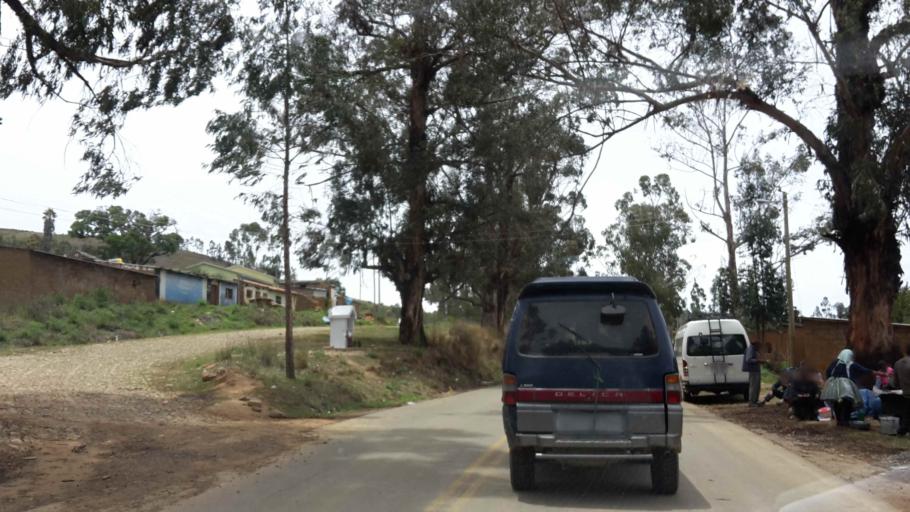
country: BO
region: Cochabamba
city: Totora
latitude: -17.7153
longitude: -65.2068
